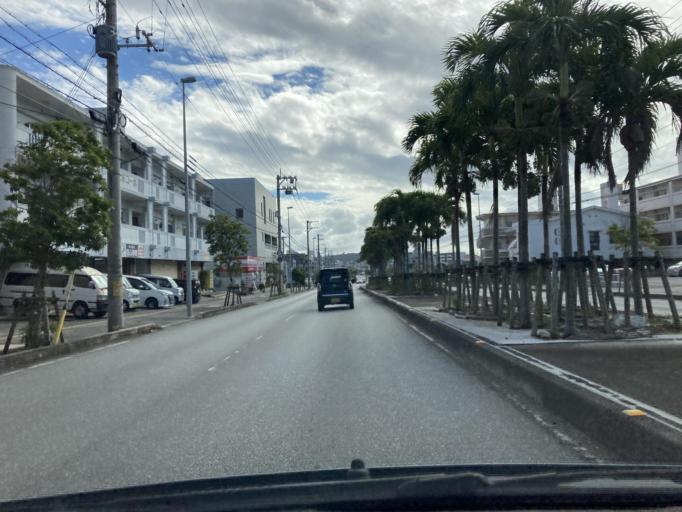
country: JP
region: Okinawa
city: Tomigusuku
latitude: 26.1619
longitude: 127.7232
